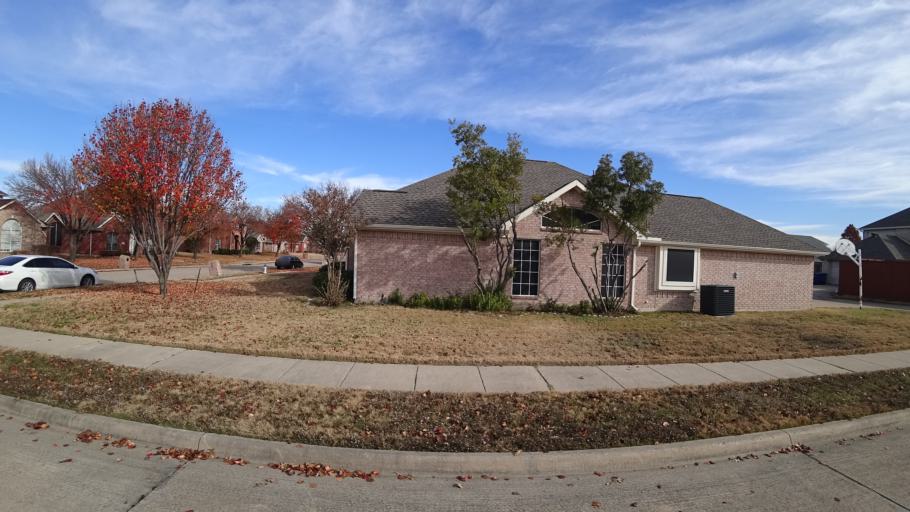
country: US
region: Texas
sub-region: Denton County
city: Lewisville
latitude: 33.0173
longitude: -96.9400
